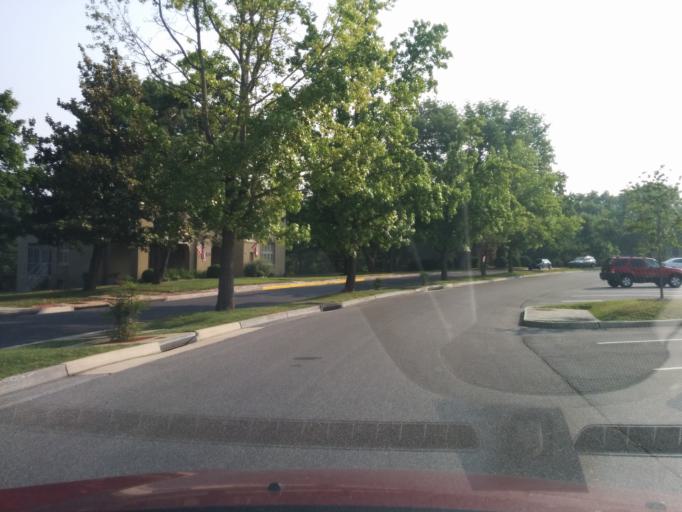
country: US
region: Virginia
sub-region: City of Lexington
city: Lexington
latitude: 37.7909
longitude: -79.4398
